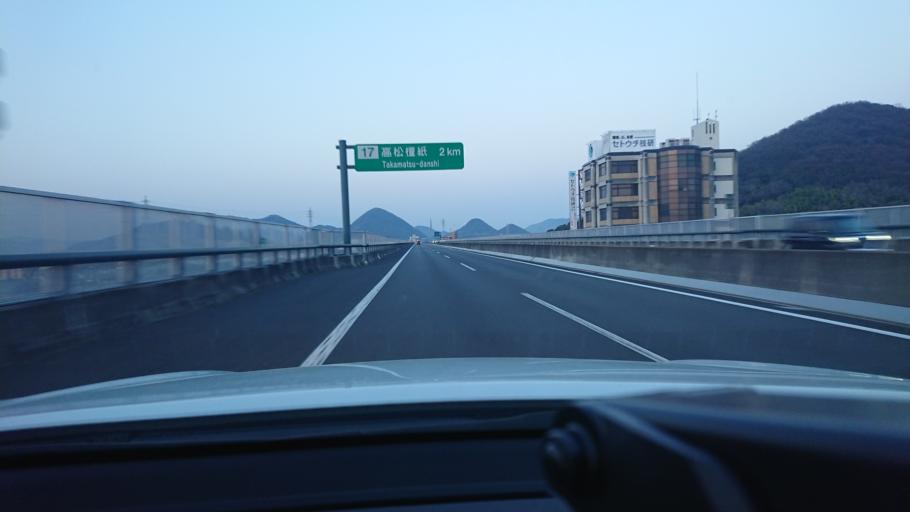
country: JP
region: Kagawa
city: Takamatsu-shi
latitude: 34.3114
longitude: 134.0248
